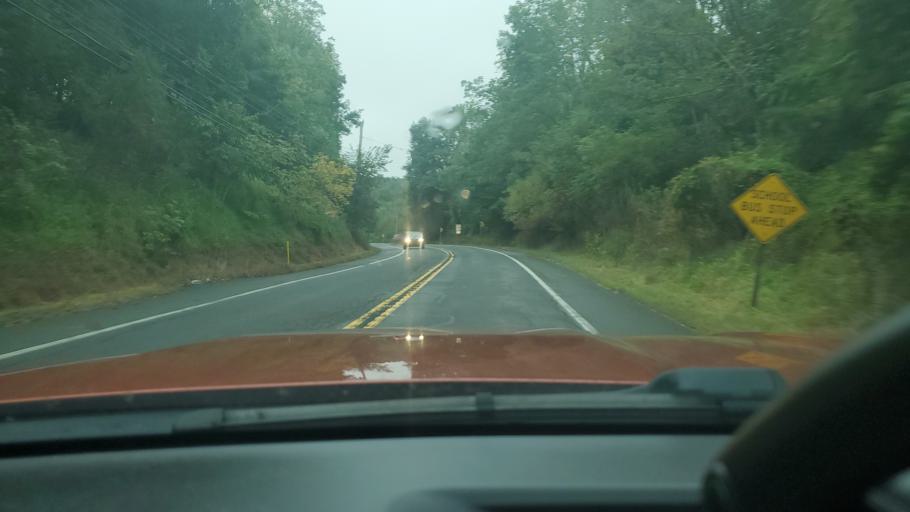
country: US
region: Pennsylvania
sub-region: Montgomery County
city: Woxall
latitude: 40.3221
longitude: -75.4813
